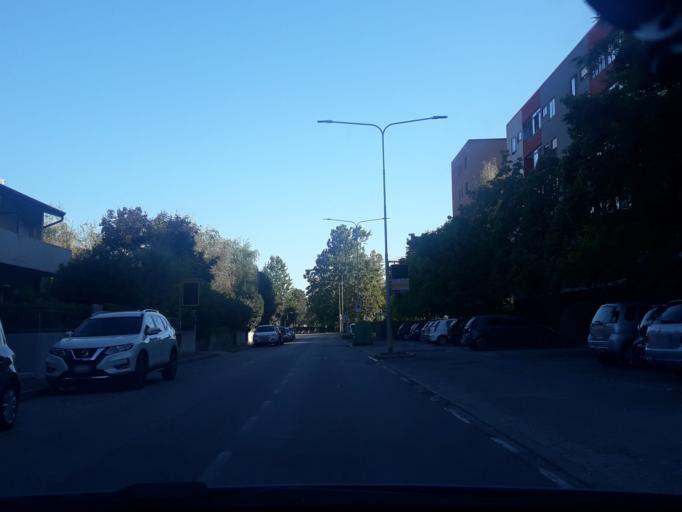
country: IT
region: Friuli Venezia Giulia
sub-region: Provincia di Udine
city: Passons
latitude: 46.0713
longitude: 13.2056
